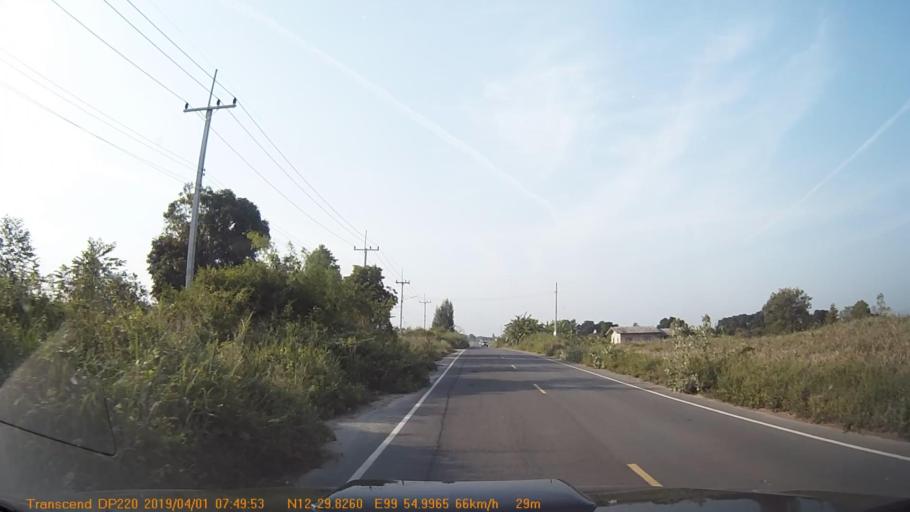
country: TH
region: Prachuap Khiri Khan
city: Hua Hin
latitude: 12.4969
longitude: 99.9166
